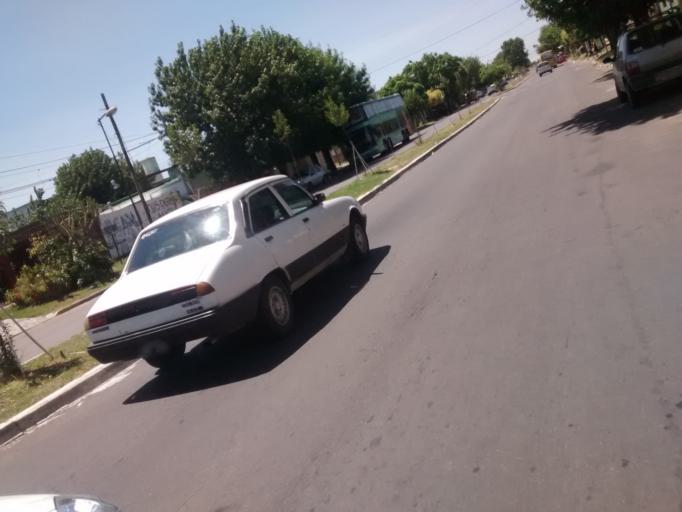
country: AR
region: Buenos Aires
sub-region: Partido de La Plata
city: La Plata
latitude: -34.9304
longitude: -57.9152
